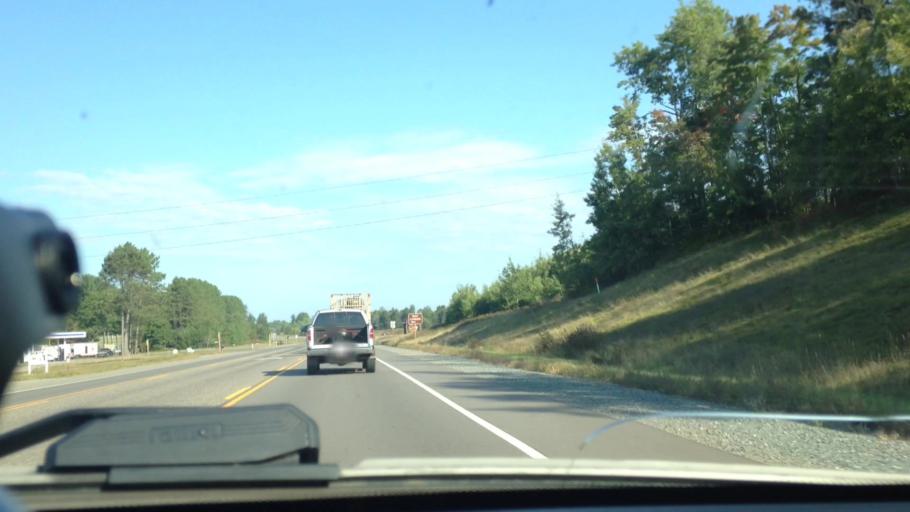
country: US
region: Michigan
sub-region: Dickinson County
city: Iron Mountain
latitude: 45.8695
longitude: -88.0823
